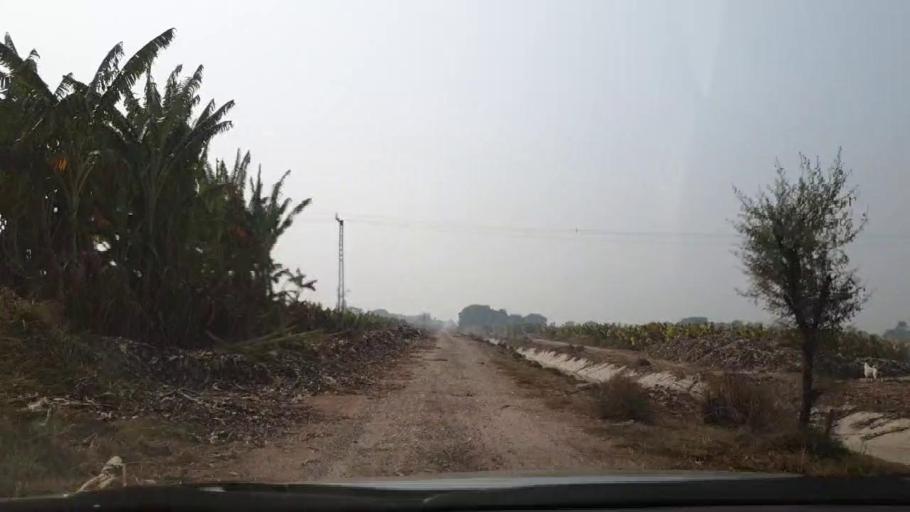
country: PK
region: Sindh
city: Matiari
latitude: 25.6364
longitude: 68.5096
